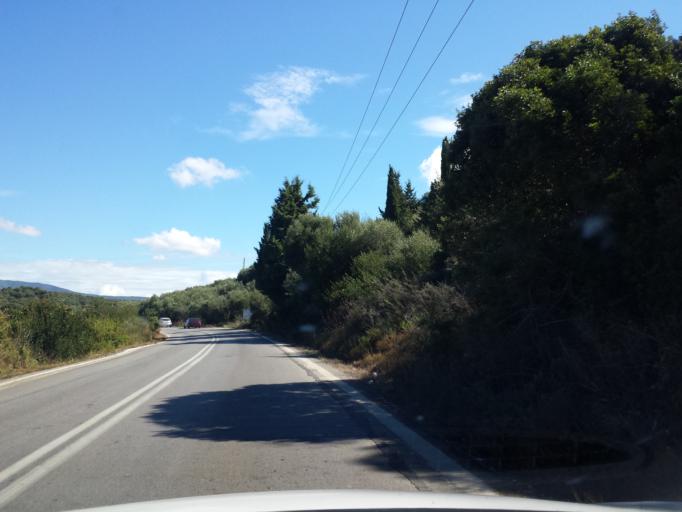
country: GR
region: Peloponnese
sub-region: Nomos Messinias
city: Pylos
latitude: 36.9253
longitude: 21.7152
